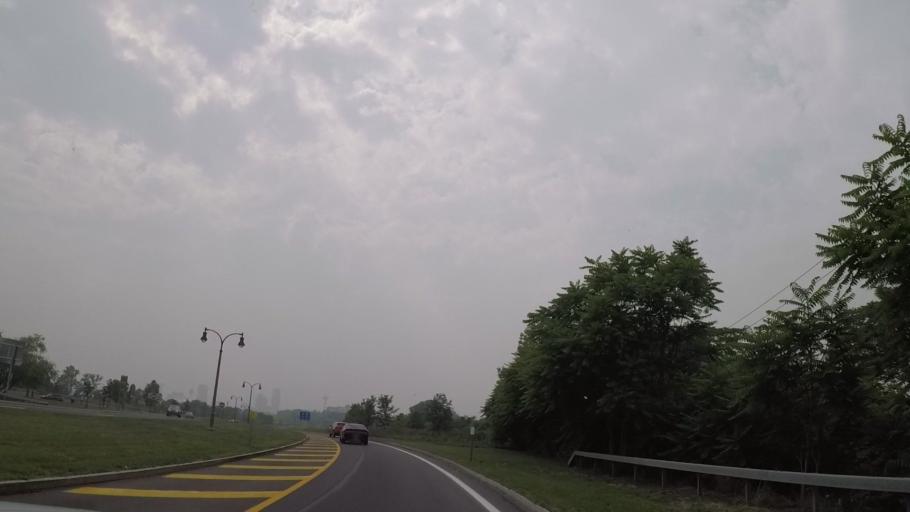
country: US
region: New York
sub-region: Niagara County
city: Niagara Falls
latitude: 43.0801
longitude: -79.0465
